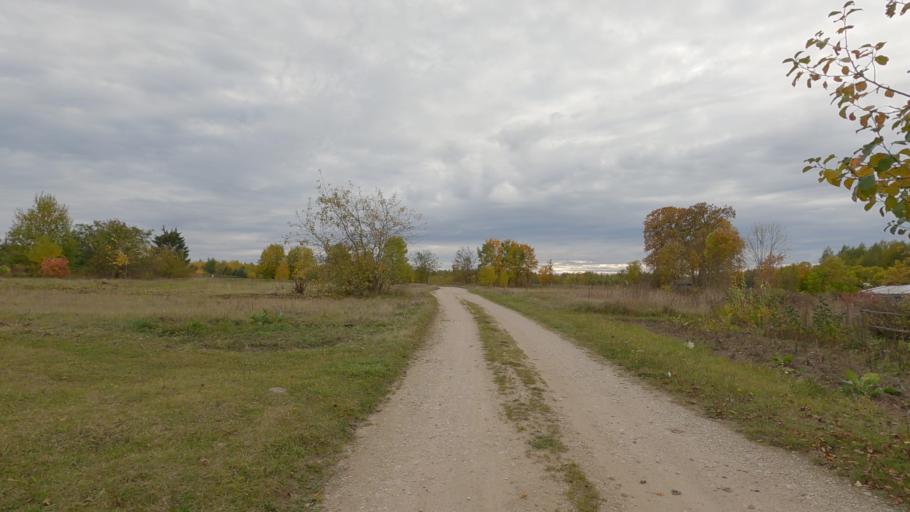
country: EE
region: Raplamaa
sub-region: Rapla vald
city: Rapla
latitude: 58.9972
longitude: 24.7807
